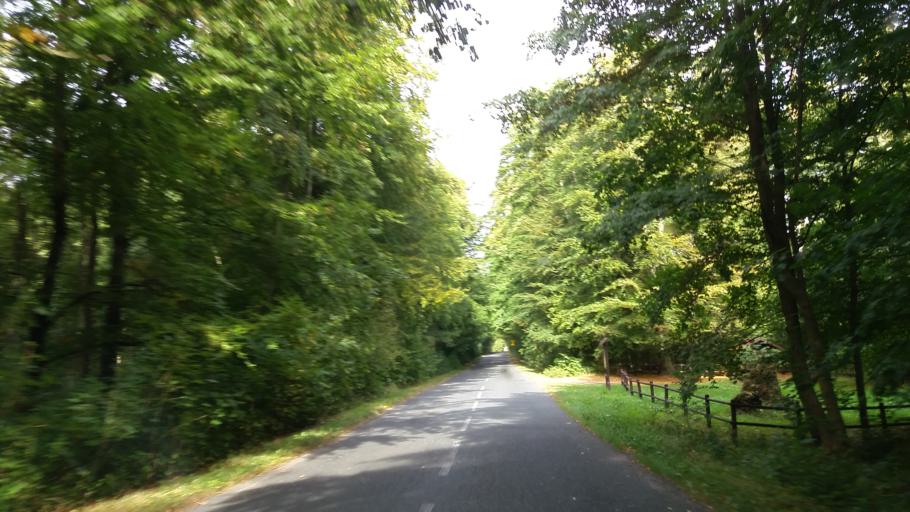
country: PL
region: West Pomeranian Voivodeship
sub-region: Powiat choszczenski
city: Krzecin
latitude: 53.0177
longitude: 15.5079
